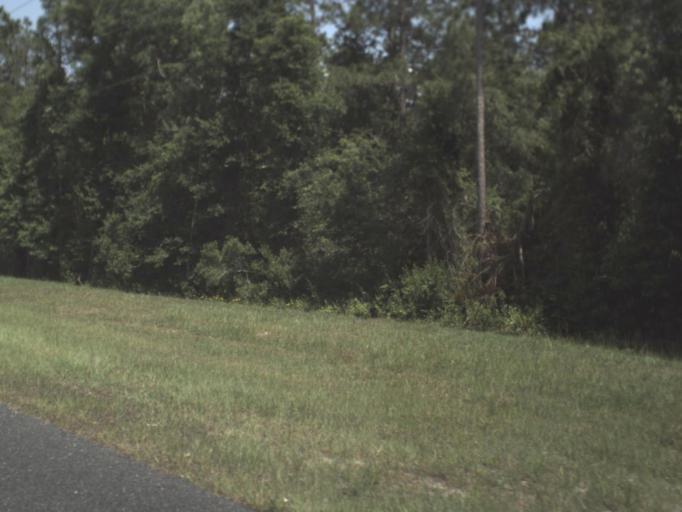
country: US
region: Florida
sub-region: Alachua County
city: Hawthorne
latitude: 29.5987
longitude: -82.1703
